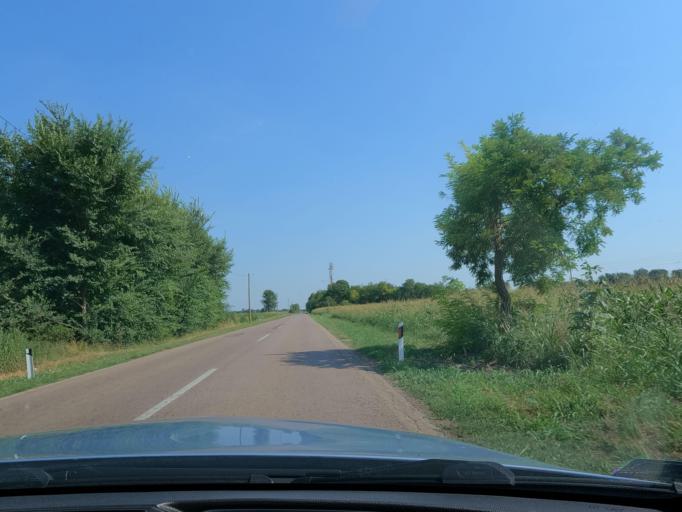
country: RS
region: Autonomna Pokrajina Vojvodina
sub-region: Severnobacki Okrug
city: Mali Igos
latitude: 45.7711
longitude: 19.7340
